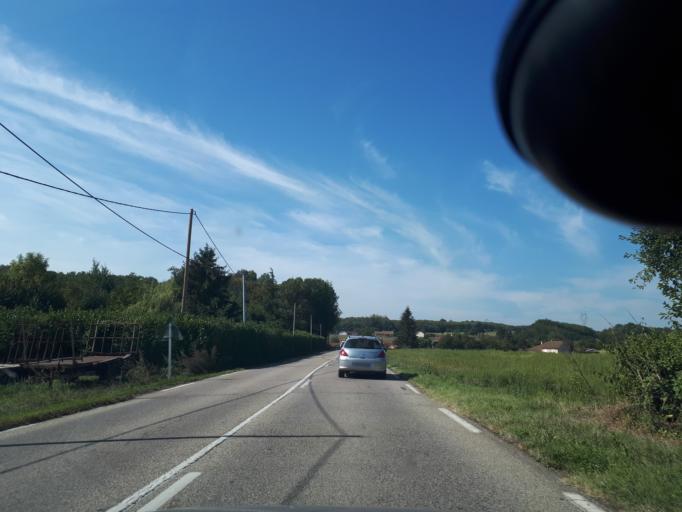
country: FR
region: Rhone-Alpes
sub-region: Departement de l'Isere
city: Chatonnay
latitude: 45.5340
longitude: 5.2249
